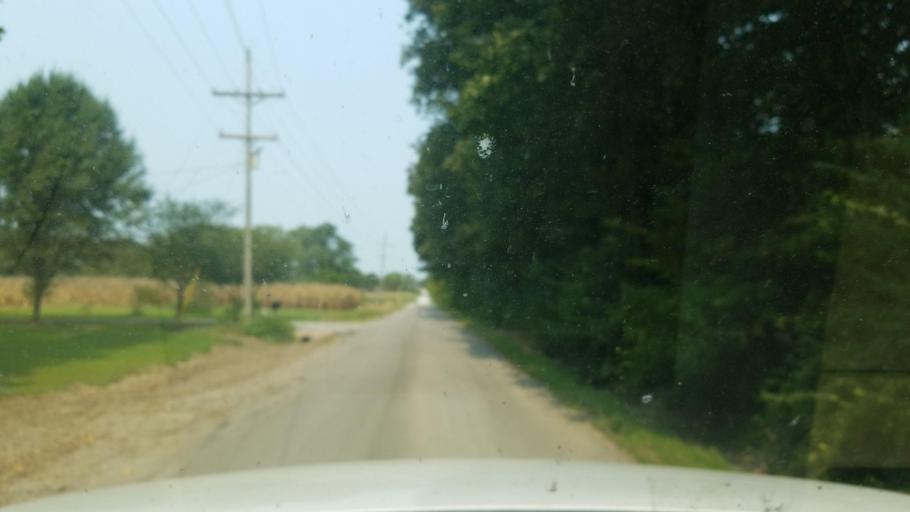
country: US
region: Illinois
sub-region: Saline County
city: Harrisburg
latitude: 37.8092
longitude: -88.5167
